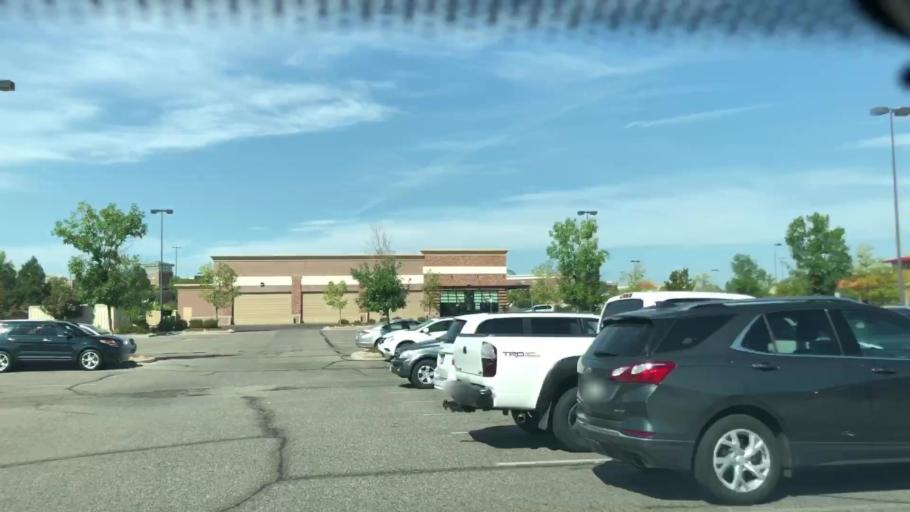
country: US
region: Colorado
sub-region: Douglas County
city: Parker
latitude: 39.6008
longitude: -104.7056
